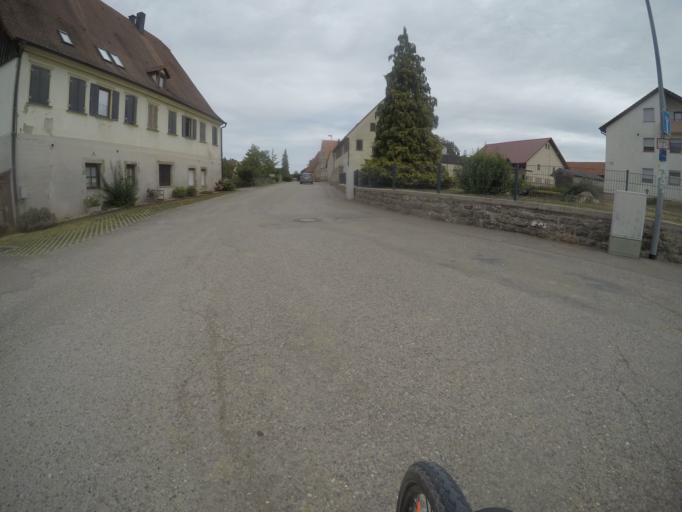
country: DE
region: Baden-Wuerttemberg
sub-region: Regierungsbezirk Stuttgart
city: Oberriexingen
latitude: 48.9060
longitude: 9.0232
